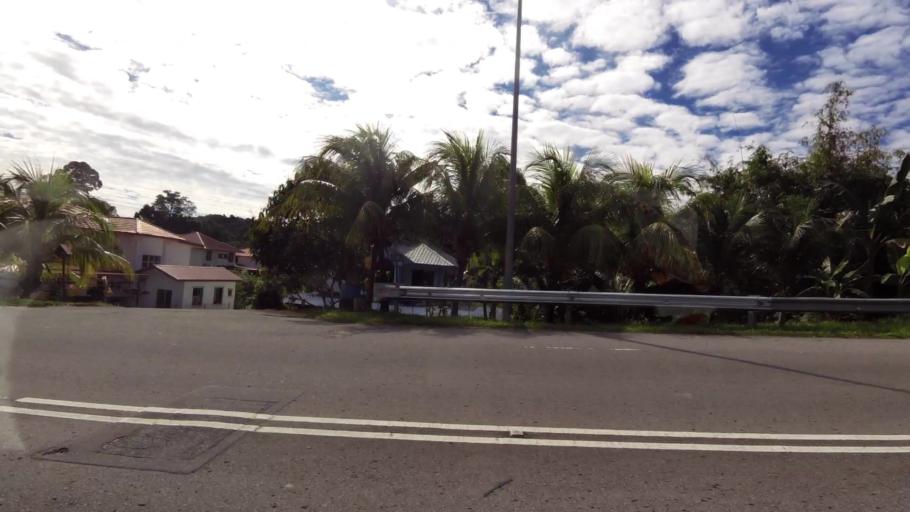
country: BN
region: Brunei and Muara
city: Bandar Seri Begawan
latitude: 4.9032
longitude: 114.9762
